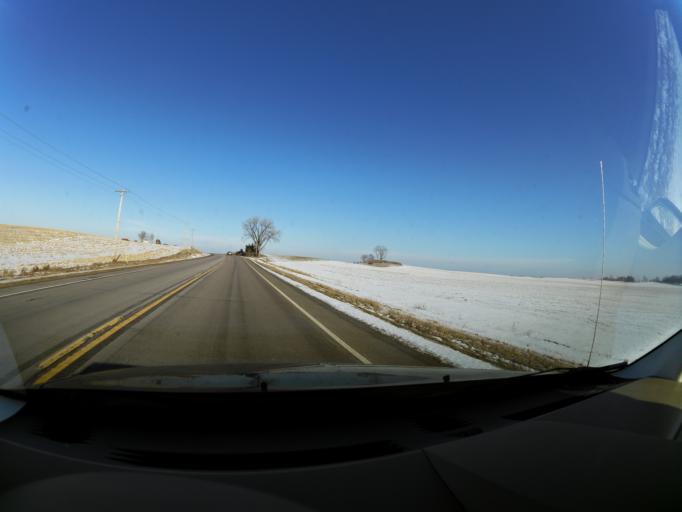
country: US
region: Minnesota
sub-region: Goodhue County
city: Cannon Falls
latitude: 44.5478
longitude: -92.8852
